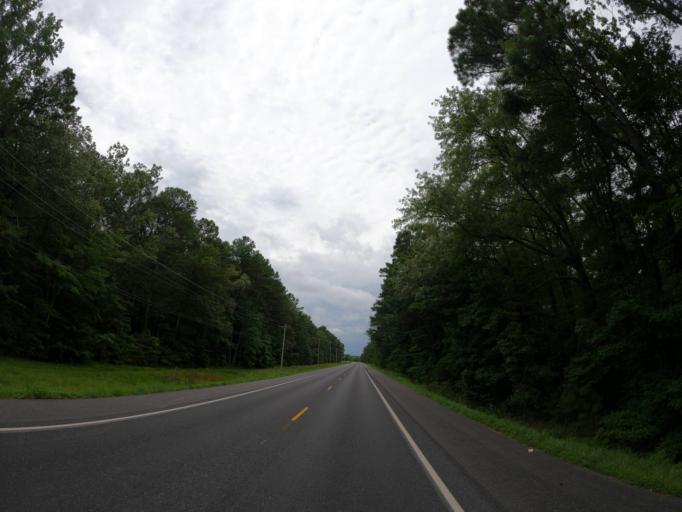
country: US
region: Maryland
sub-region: Saint Mary's County
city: Lexington Park
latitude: 38.1758
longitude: -76.5216
